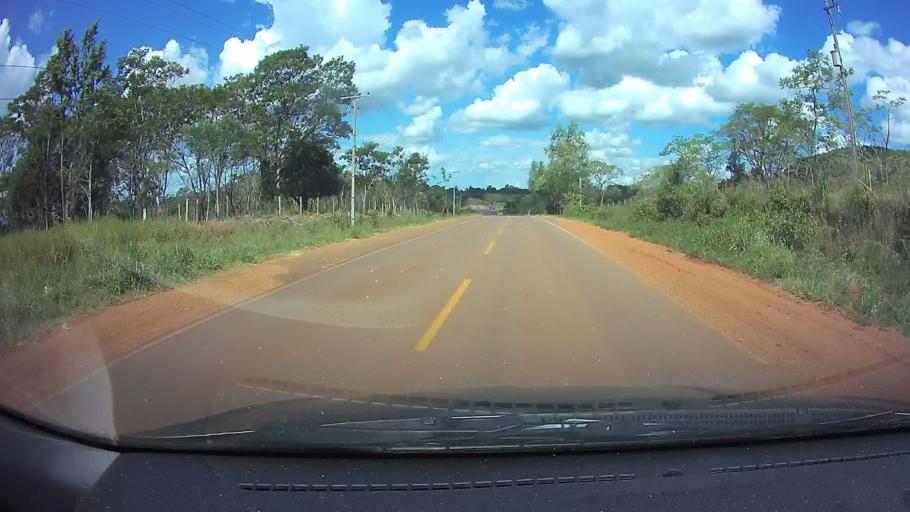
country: PY
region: Paraguari
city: La Colmena
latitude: -25.9168
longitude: -56.7385
